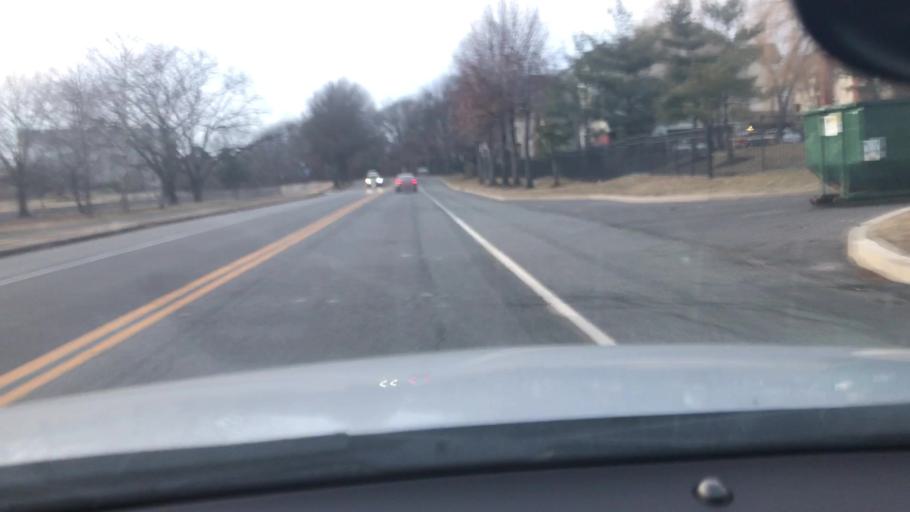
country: US
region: New Jersey
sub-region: Camden County
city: Collingswood
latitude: 39.9282
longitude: -75.0608
